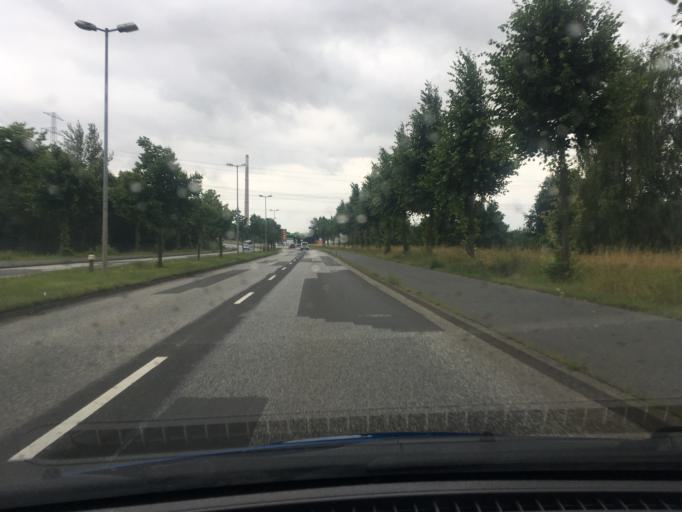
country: DE
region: Mecklenburg-Vorpommern
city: Feldstadt
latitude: 53.5882
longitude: 11.4016
